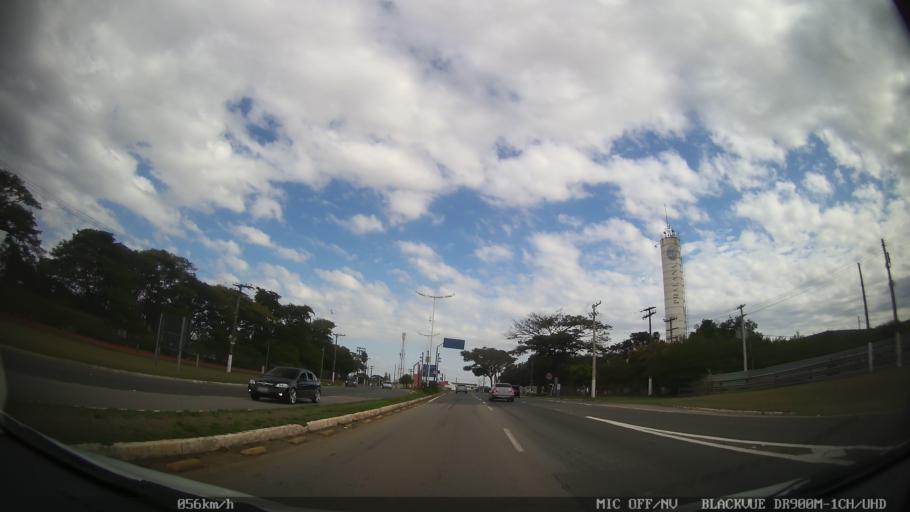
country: BR
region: Sao Paulo
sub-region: Limeira
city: Limeira
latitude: -22.5481
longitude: -47.3782
